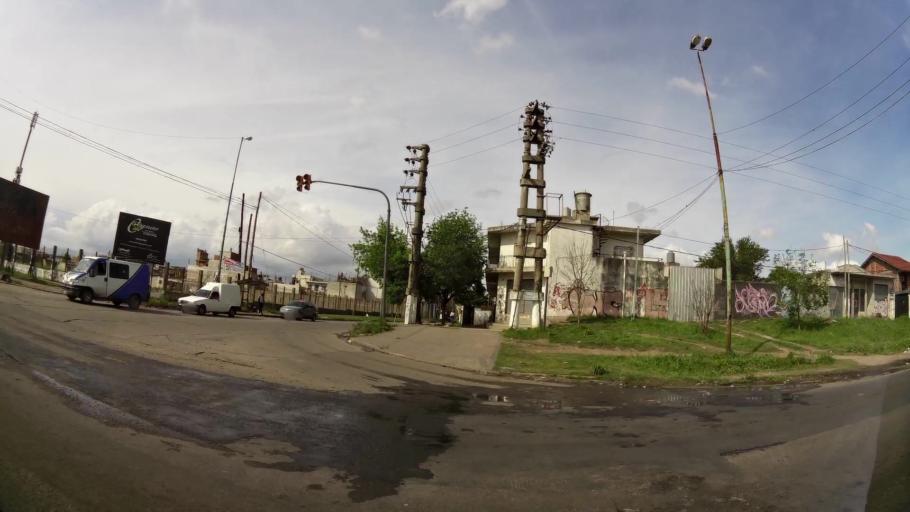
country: AR
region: Buenos Aires
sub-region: Partido de Quilmes
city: Quilmes
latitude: -34.7648
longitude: -58.2503
